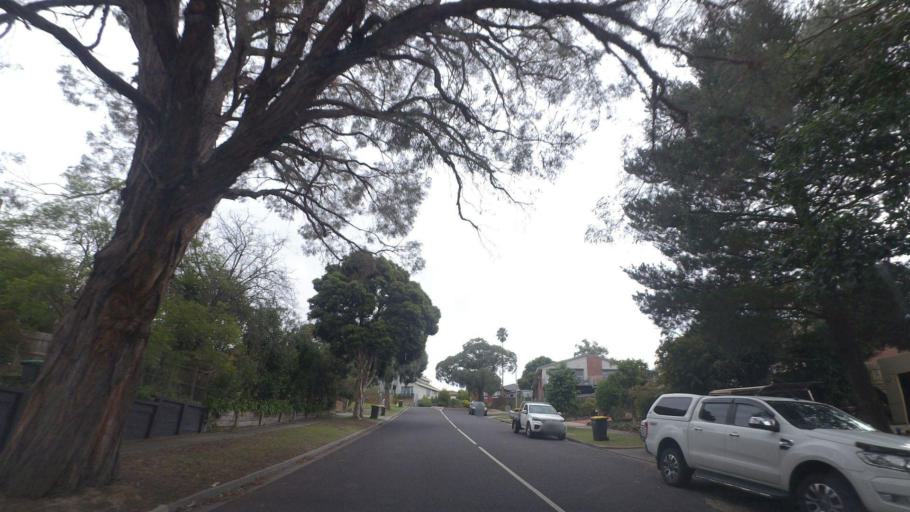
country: AU
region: Victoria
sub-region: Nillumbik
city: Eltham
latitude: -37.7542
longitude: 145.1566
